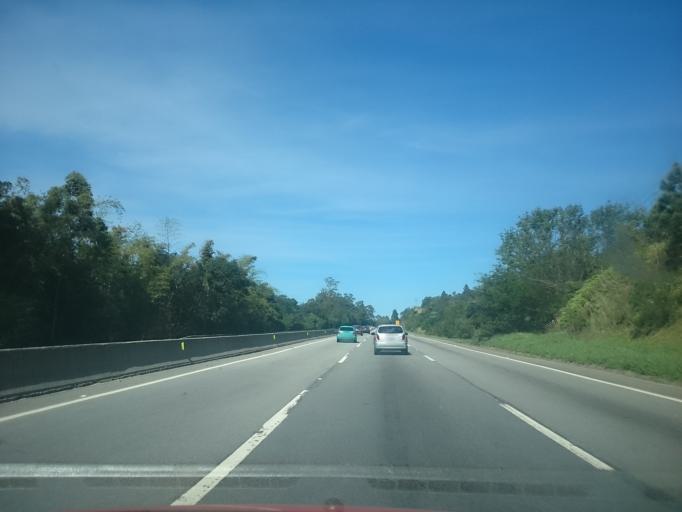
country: BR
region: Santa Catarina
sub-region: Palhoca
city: Palhoca
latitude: -27.7101
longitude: -48.6541
